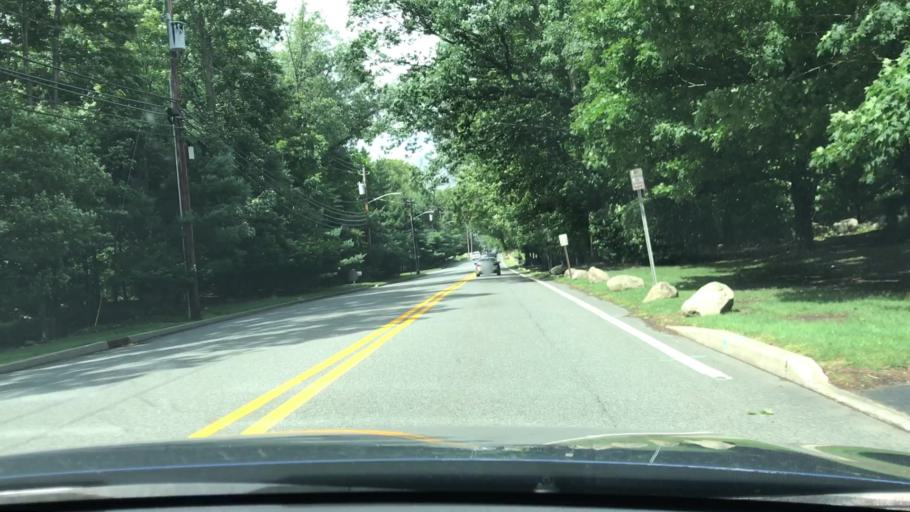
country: US
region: New Jersey
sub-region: Bergen County
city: Wyckoff
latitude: 41.0312
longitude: -74.1680
